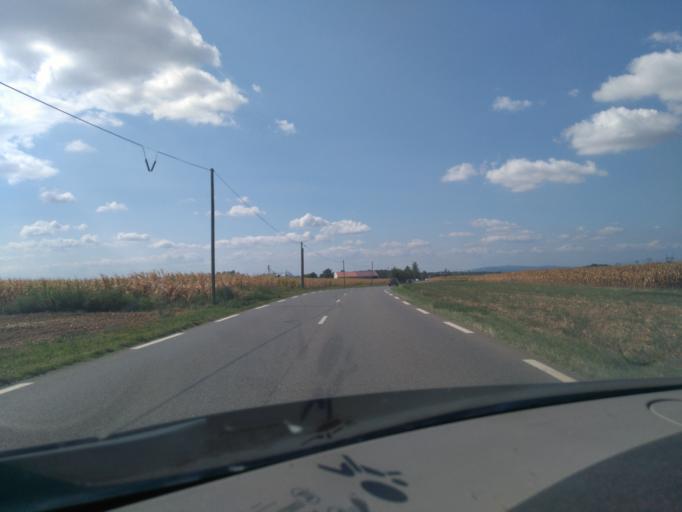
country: FR
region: Rhone-Alpes
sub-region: Departement du Rhone
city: Saint-Laurent-de-Mure
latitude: 45.7214
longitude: 5.0473
